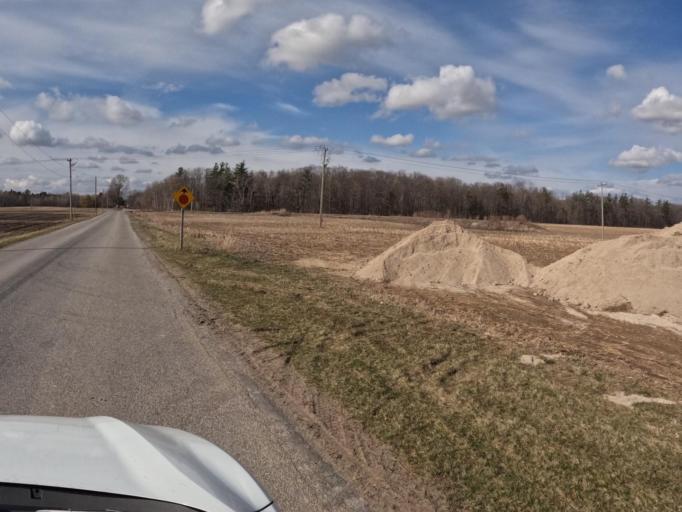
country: CA
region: Ontario
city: Norfolk County
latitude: 42.8853
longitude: -80.2836
